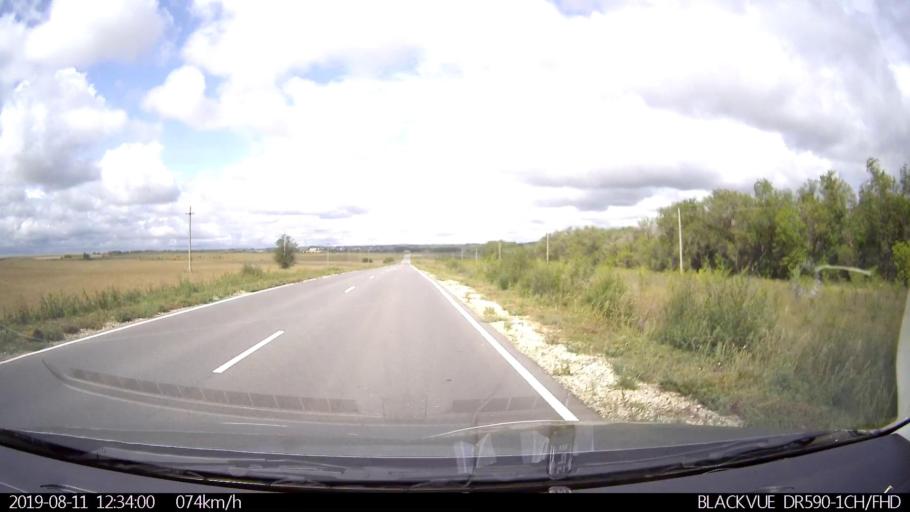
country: RU
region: Ulyanovsk
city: Ignatovka
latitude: 53.8137
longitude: 47.8485
